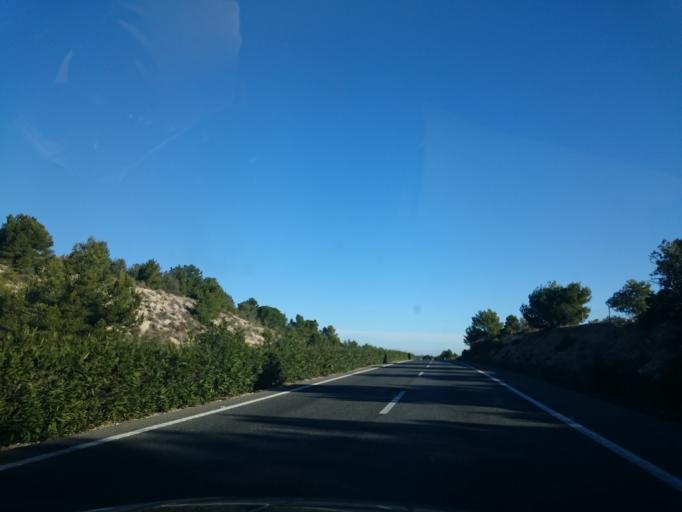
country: ES
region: Catalonia
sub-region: Provincia de Tarragona
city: El Perello
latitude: 40.8512
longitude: 0.7585
